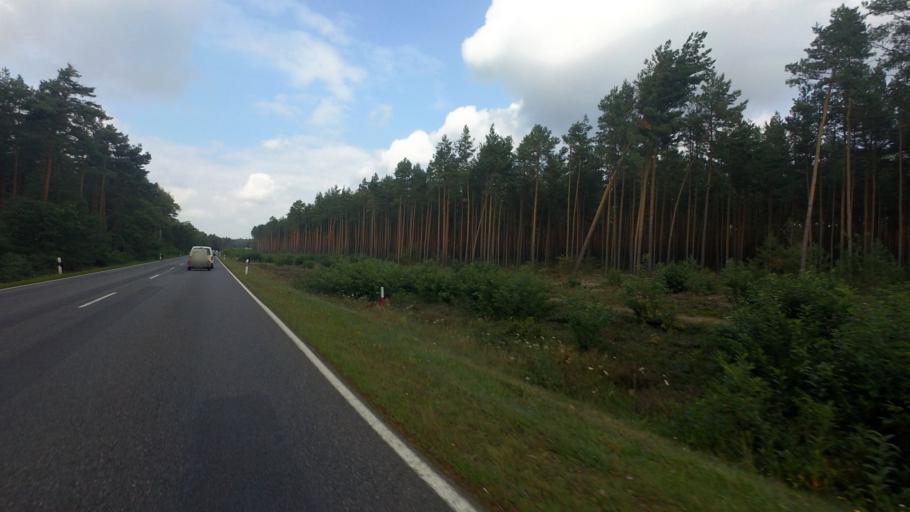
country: DE
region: Brandenburg
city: Elsterwerda
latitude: 51.4977
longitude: 13.4701
